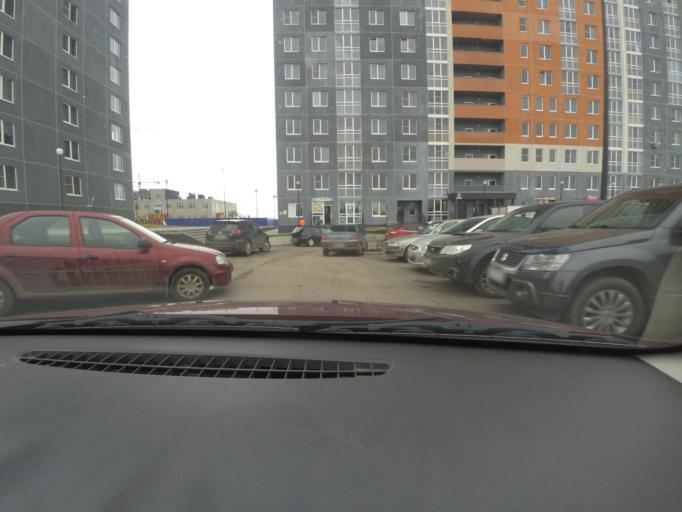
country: RU
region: Nizjnij Novgorod
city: Afonino
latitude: 56.2476
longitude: 44.0425
